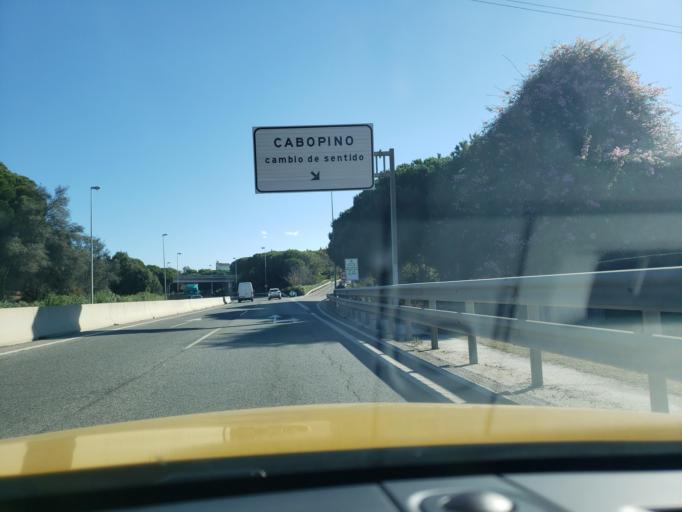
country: ES
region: Andalusia
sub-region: Provincia de Malaga
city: Fuengirola
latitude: 36.4888
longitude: -4.7452
